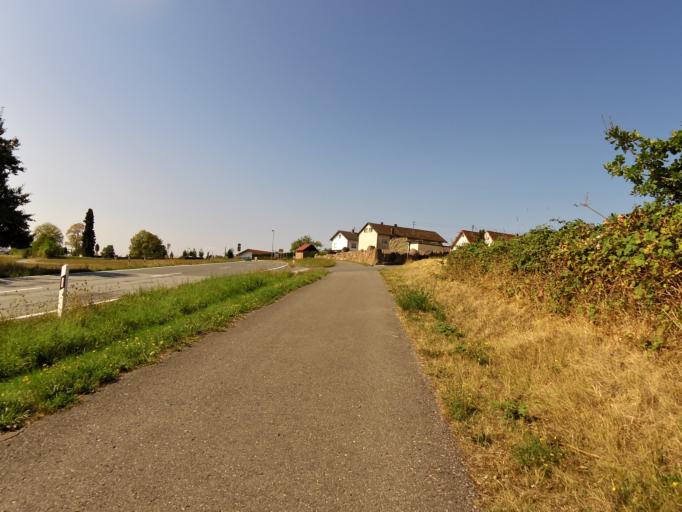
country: DE
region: Baden-Wuerttemberg
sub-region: Karlsruhe Region
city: Limbach
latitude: 49.4650
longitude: 9.2167
